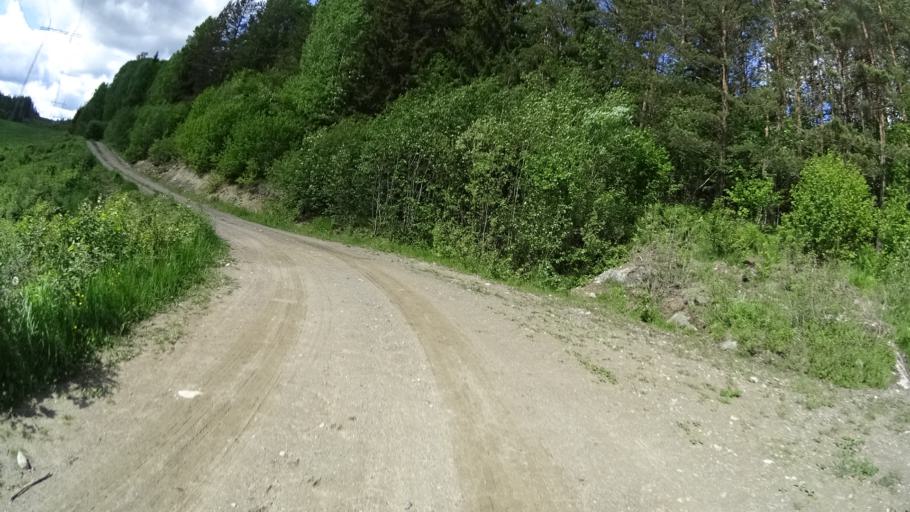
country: FI
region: Uusimaa
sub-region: Raaseporin
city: Karis
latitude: 60.1512
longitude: 23.6256
